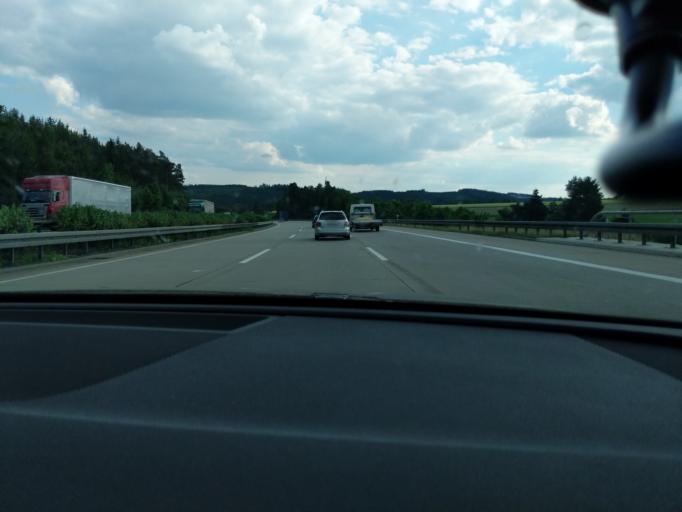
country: DE
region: Thuringia
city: Schleiz
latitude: 50.5260
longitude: 11.8002
